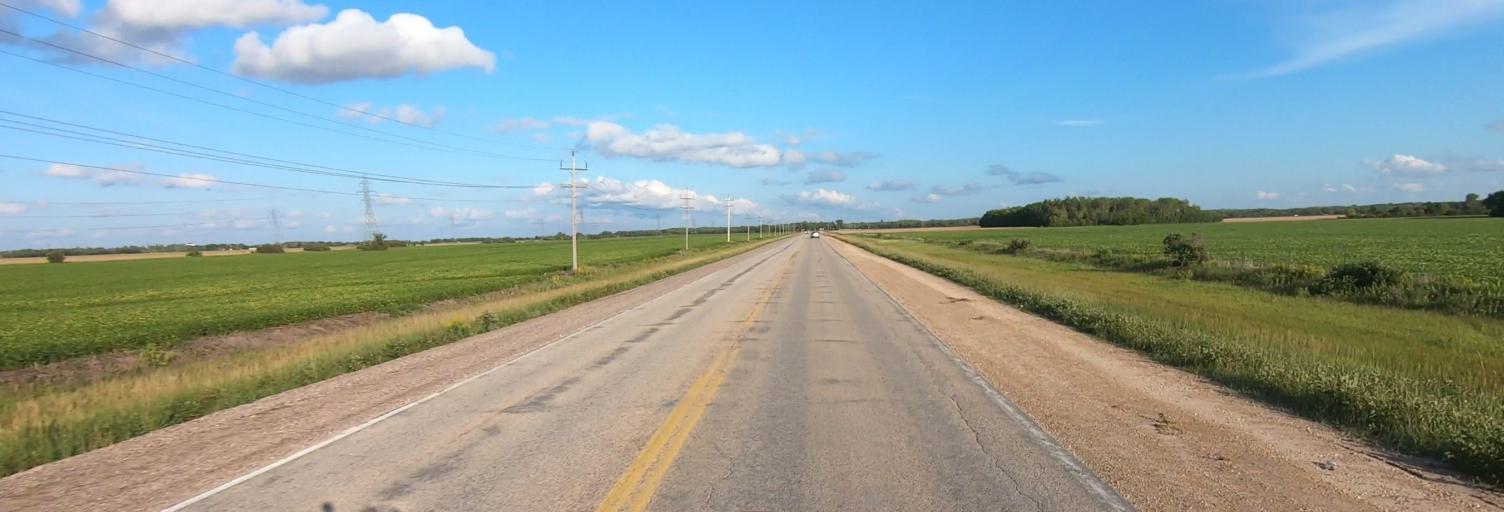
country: CA
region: Manitoba
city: Selkirk
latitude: 50.1201
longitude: -96.8545
